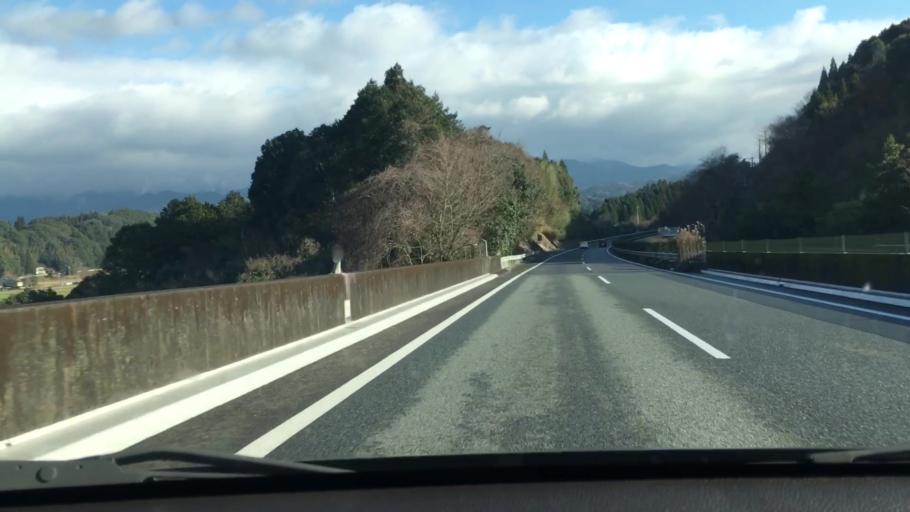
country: JP
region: Kumamoto
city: Hitoyoshi
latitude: 32.1804
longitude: 130.7846
